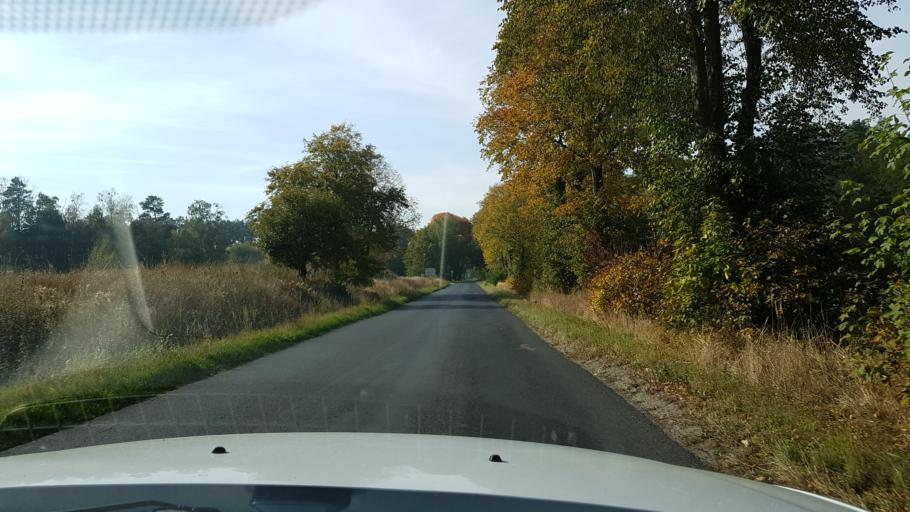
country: PL
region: West Pomeranian Voivodeship
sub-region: Powiat mysliborski
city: Barlinek
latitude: 52.9655
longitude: 15.1448
